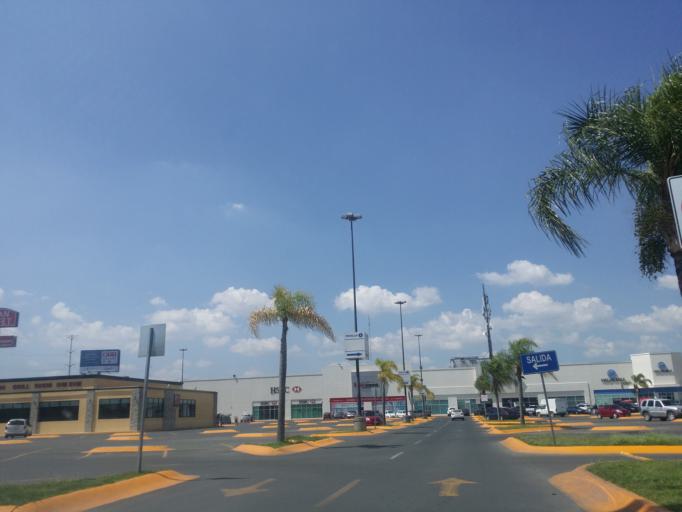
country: MX
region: Guanajuato
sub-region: Leon
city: Medina
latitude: 21.1465
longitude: -101.6482
